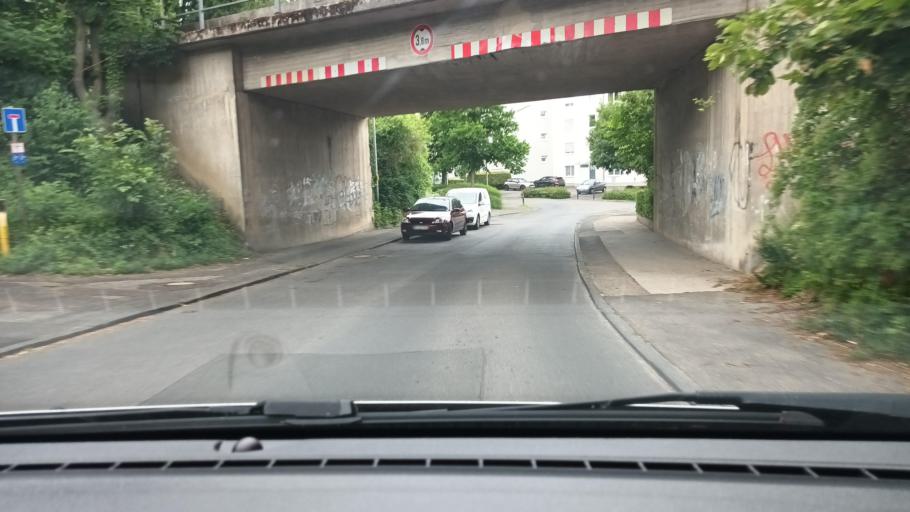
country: DE
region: North Rhine-Westphalia
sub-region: Regierungsbezirk Koln
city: Hurth
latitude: 50.8652
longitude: 6.8638
